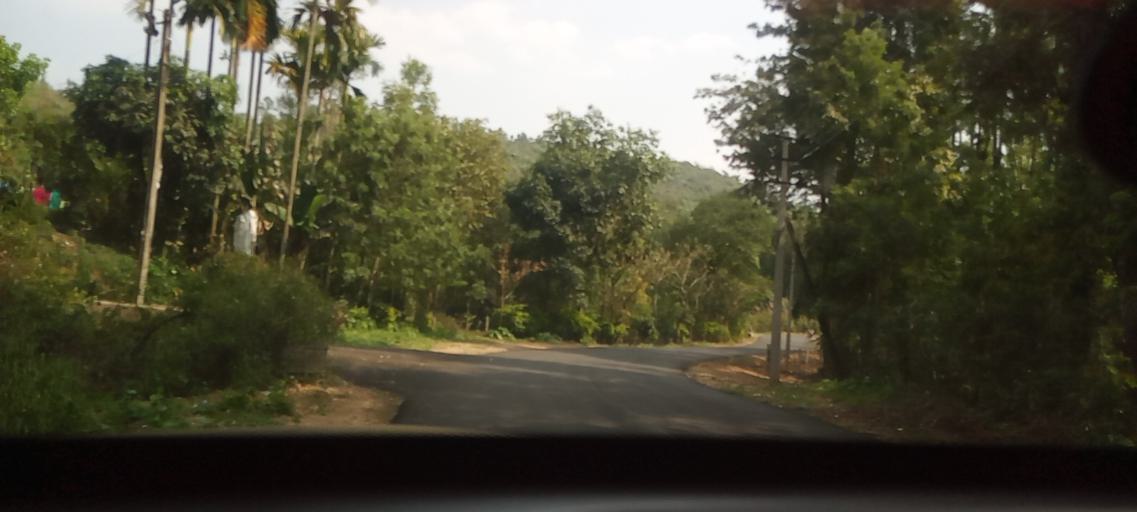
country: IN
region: Karnataka
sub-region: Chikmagalur
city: Chikmagalur
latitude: 13.2663
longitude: 75.7221
